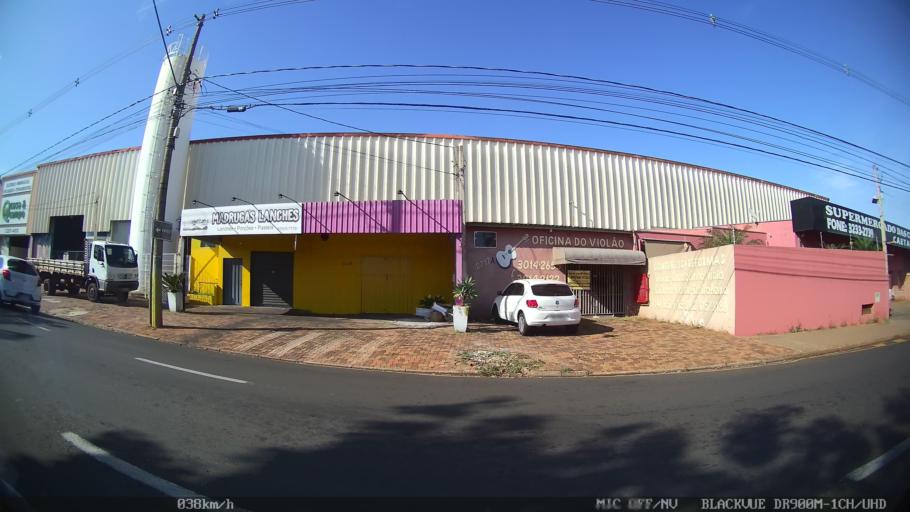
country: BR
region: Sao Paulo
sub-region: Sao Jose Do Rio Preto
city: Sao Jose do Rio Preto
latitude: -20.8098
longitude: -49.3999
